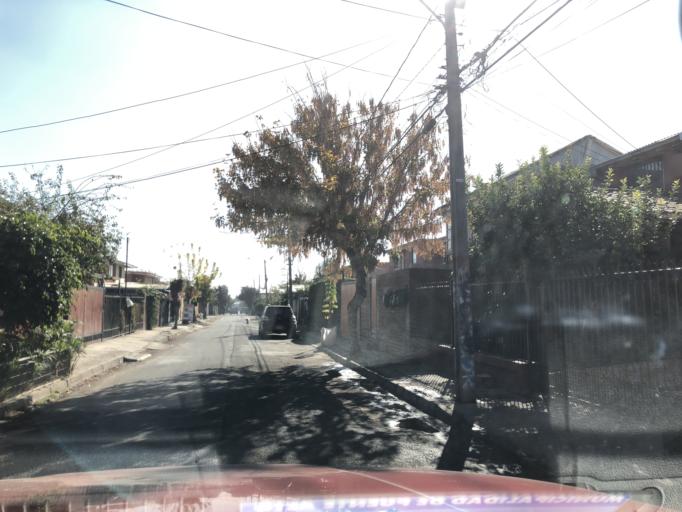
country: CL
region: Santiago Metropolitan
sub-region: Provincia de Cordillera
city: Puente Alto
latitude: -33.5706
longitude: -70.5646
